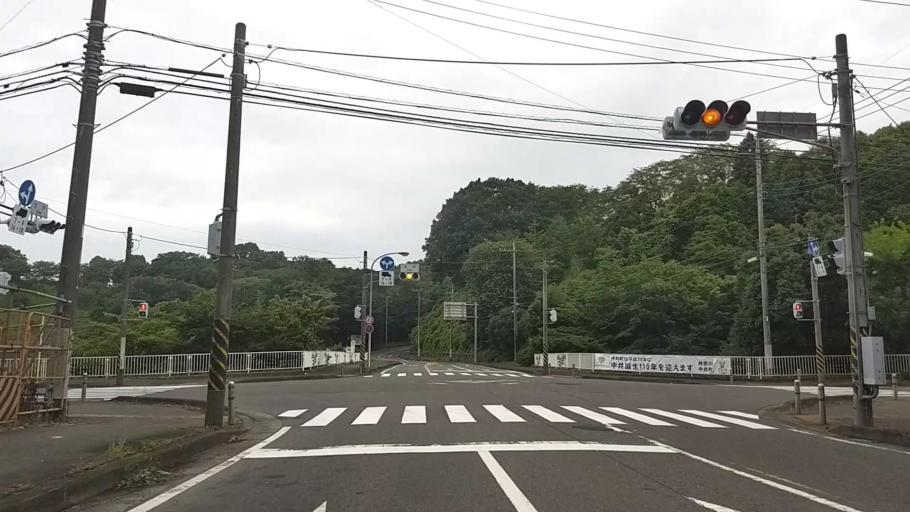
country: JP
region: Kanagawa
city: Hadano
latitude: 35.3413
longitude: 139.2223
